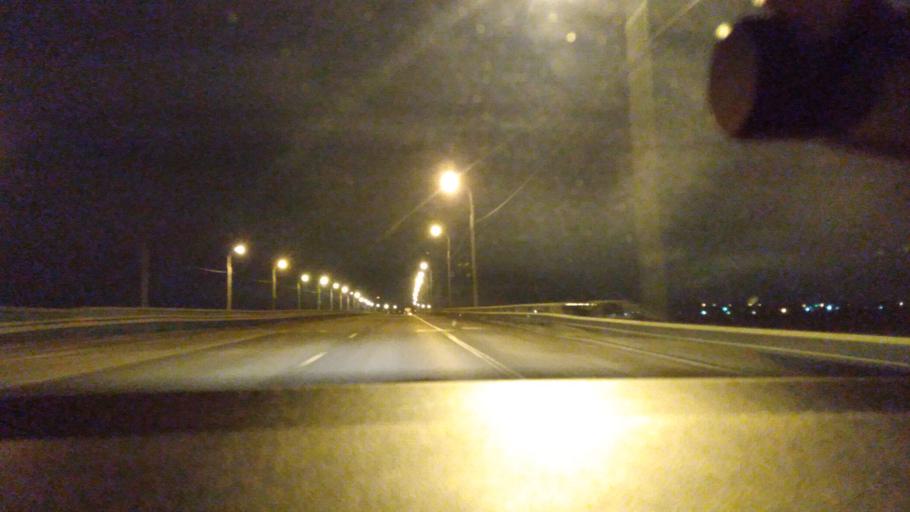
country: RU
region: Moskovskaya
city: Raduzhnyy
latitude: 55.1414
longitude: 38.7493
